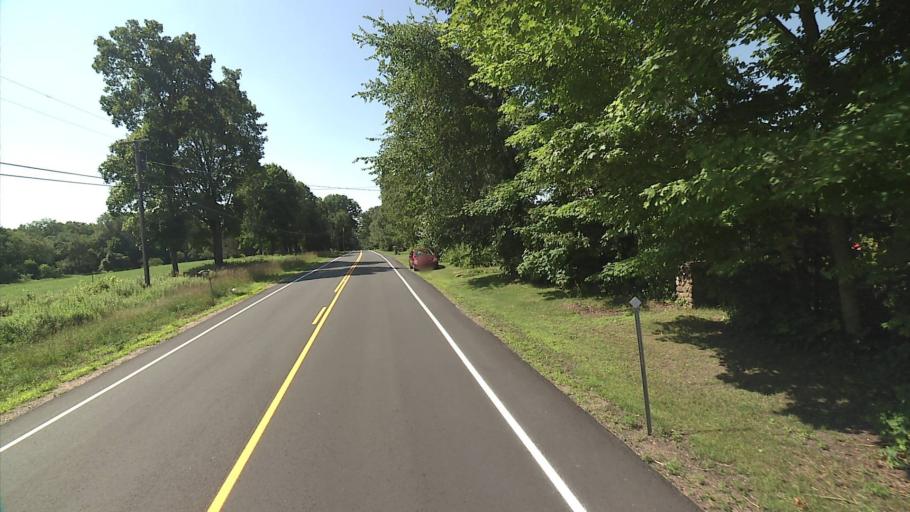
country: US
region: Connecticut
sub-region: Litchfield County
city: Northwest Harwinton
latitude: 41.7601
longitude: -73.0249
